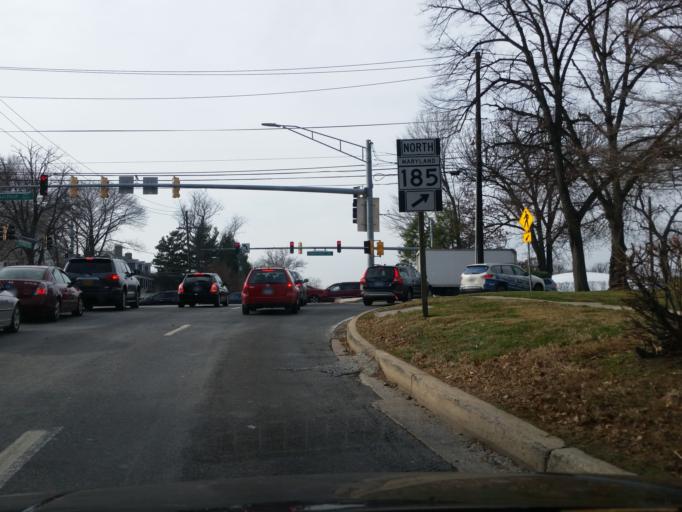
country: US
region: Maryland
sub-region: Montgomery County
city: Chevy Chase
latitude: 38.9880
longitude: -77.0766
